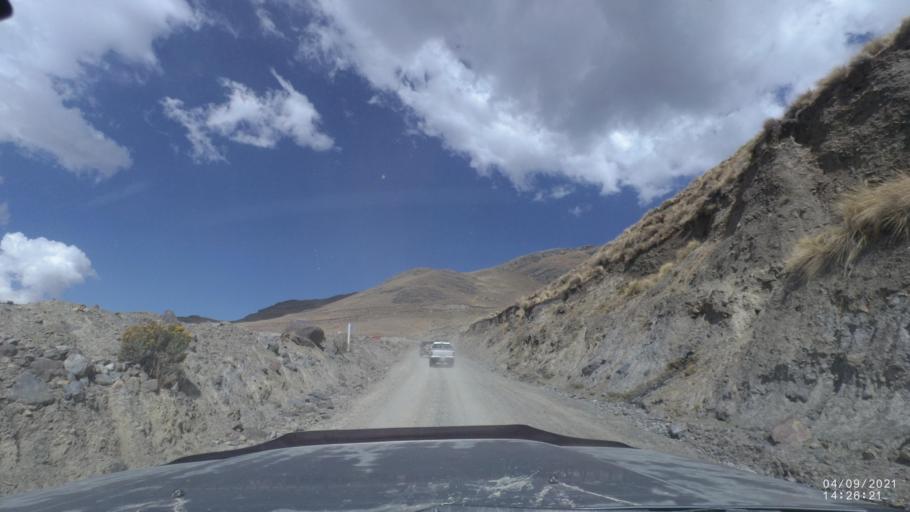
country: BO
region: Cochabamba
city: Sipe Sipe
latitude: -17.2435
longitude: -66.4090
